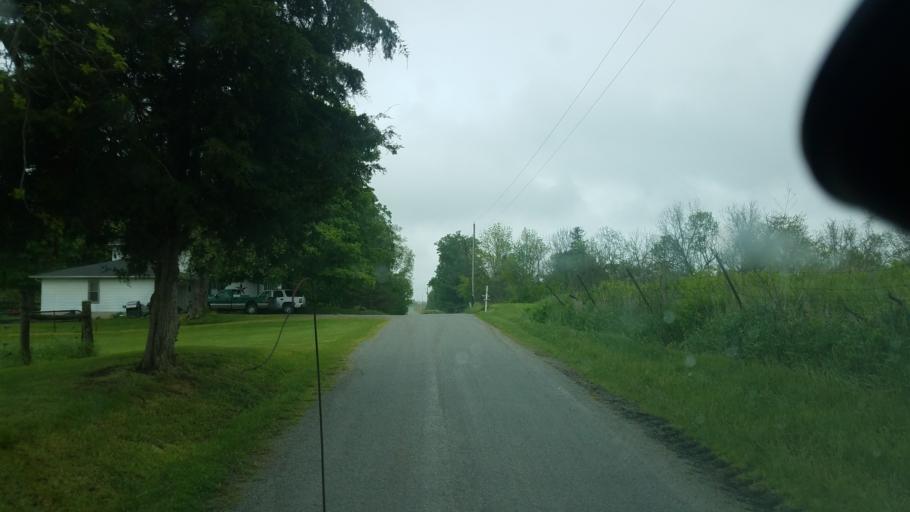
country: US
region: Ohio
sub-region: Highland County
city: Greenfield
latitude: 39.3290
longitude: -83.4529
